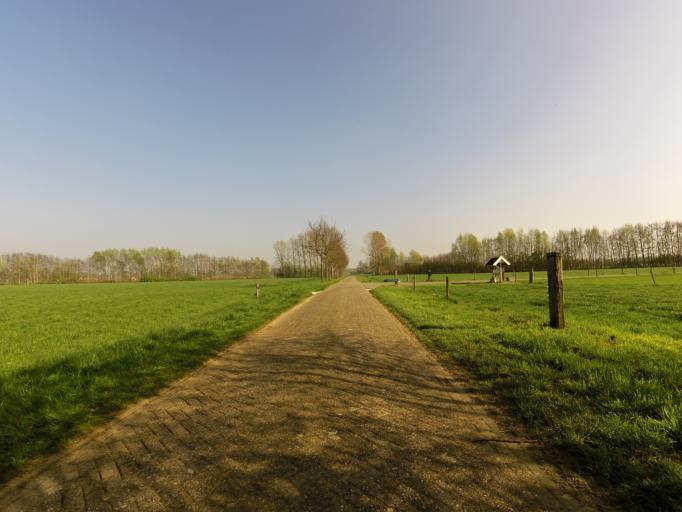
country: NL
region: Gelderland
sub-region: Gemeente Bronckhorst
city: Hengelo
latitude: 52.0192
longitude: 6.2771
